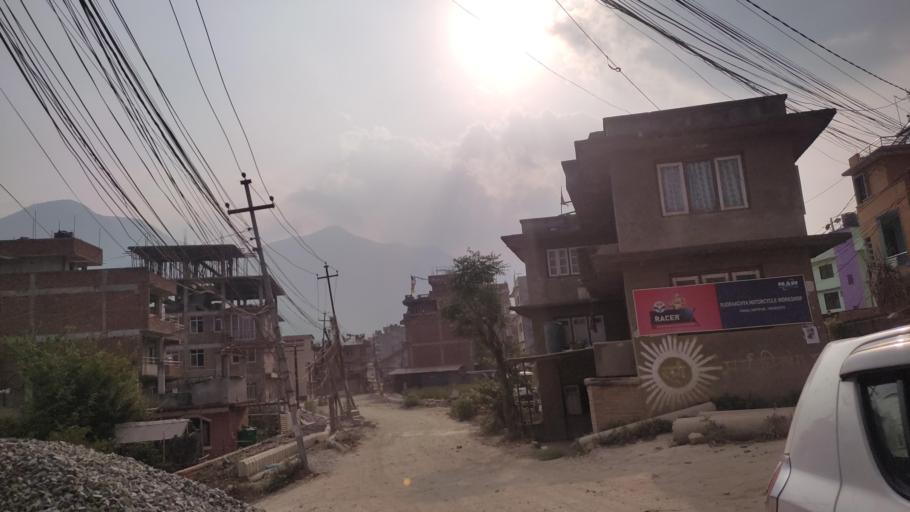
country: NP
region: Central Region
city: Kirtipur
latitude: 27.6685
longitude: 85.2801
